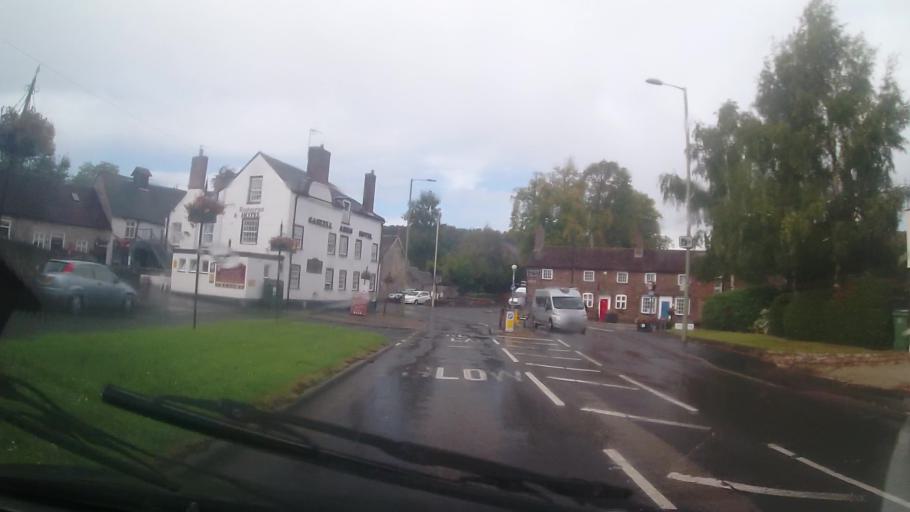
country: GB
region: England
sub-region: Shropshire
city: Much Wenlock
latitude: 52.5944
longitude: -2.5605
